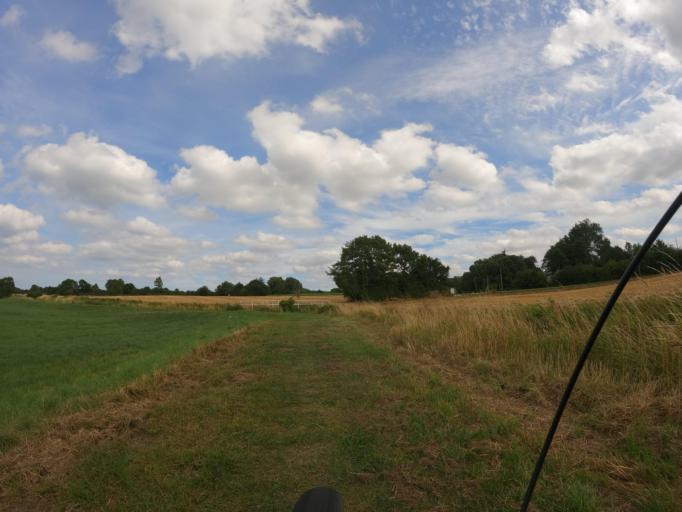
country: DE
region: Schleswig-Holstein
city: Niesgrau
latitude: 54.7550
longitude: 9.8248
